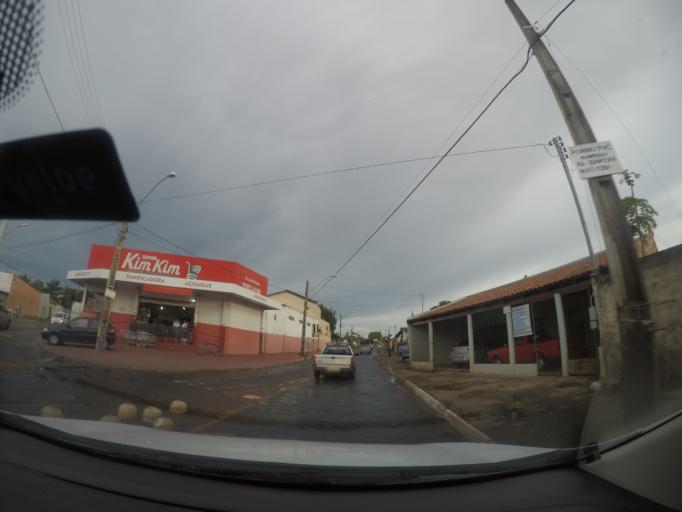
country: BR
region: Goias
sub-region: Goiania
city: Goiania
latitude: -16.7203
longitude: -49.3103
